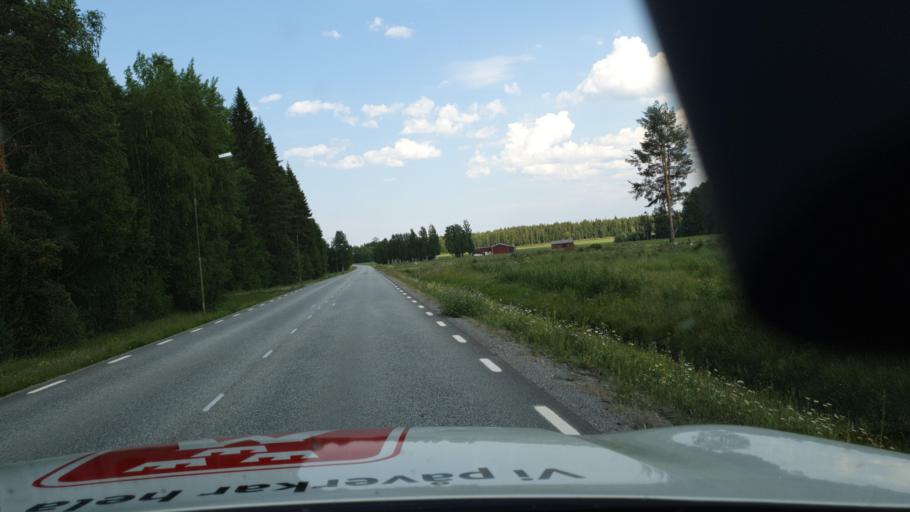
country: SE
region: Vaesterbotten
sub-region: Skelleftea Kommun
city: Viken
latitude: 64.7421
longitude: 20.8136
